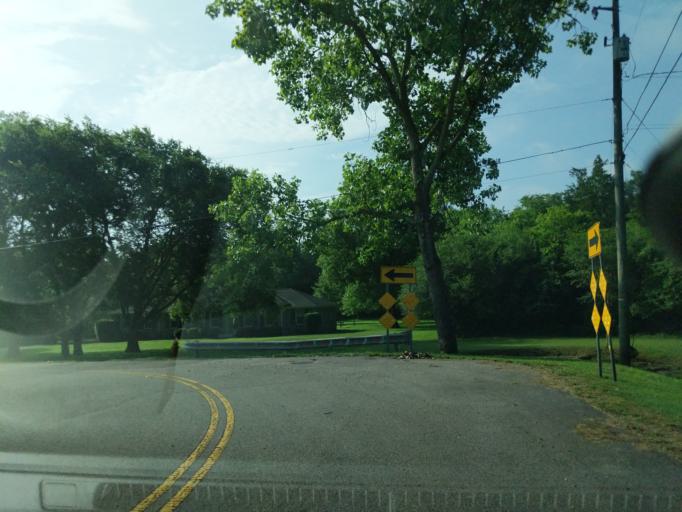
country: US
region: Tennessee
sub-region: Davidson County
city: Goodlettsville
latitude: 36.3037
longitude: -86.6739
